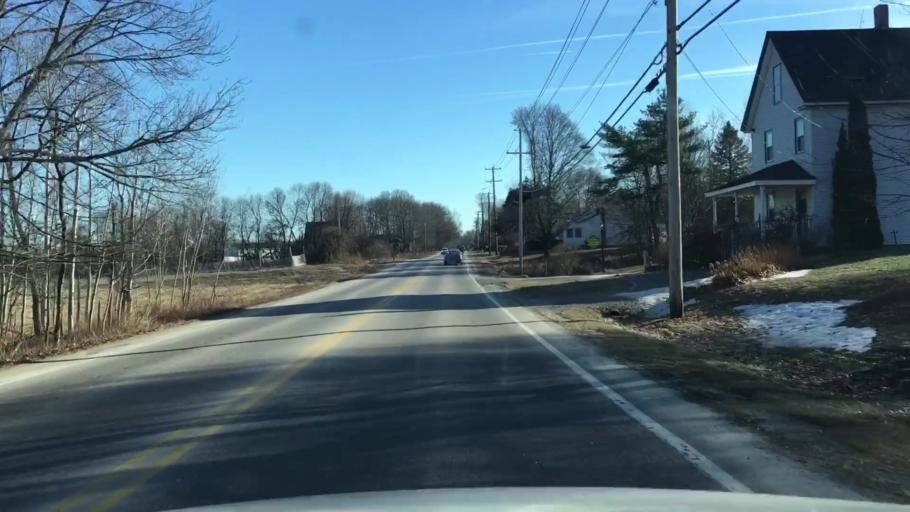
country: US
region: Maine
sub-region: Penobscot County
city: Bangor
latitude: 44.8210
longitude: -68.8047
